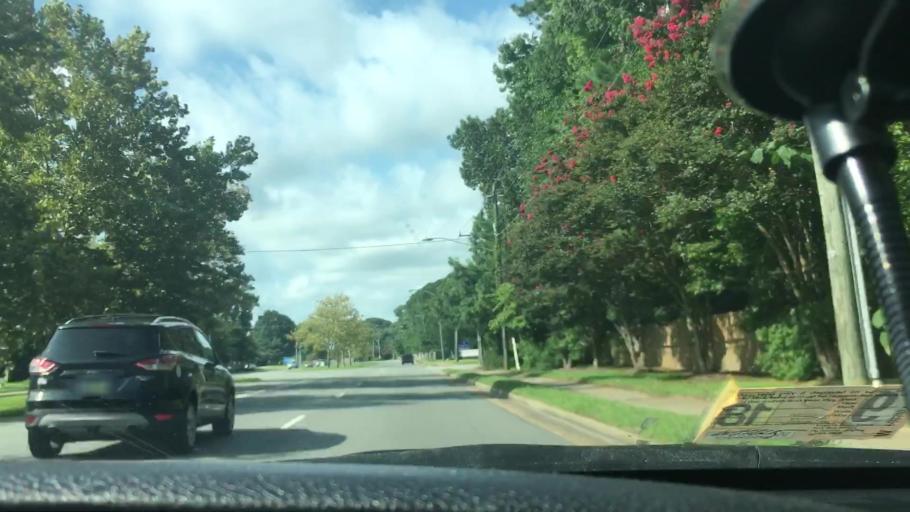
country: US
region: Virginia
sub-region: City of Virginia Beach
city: Virginia Beach
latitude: 36.8669
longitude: -76.0438
